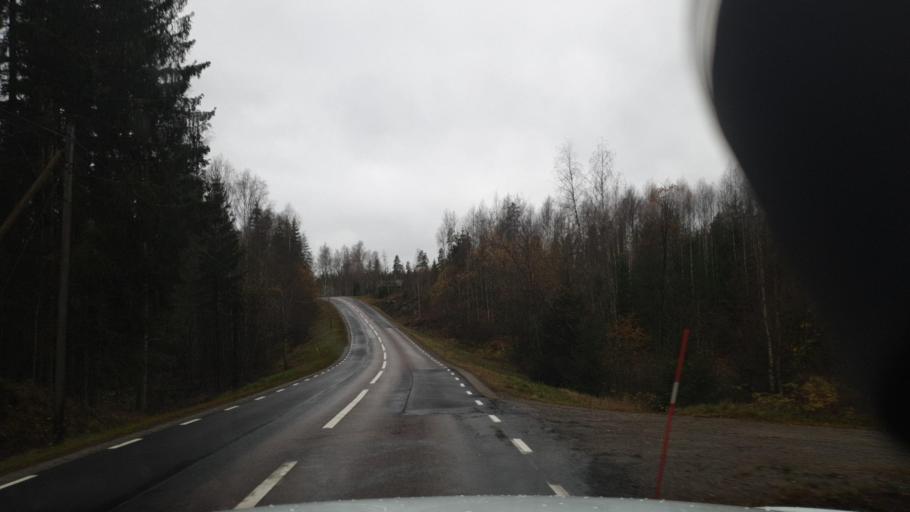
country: SE
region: Vaermland
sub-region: Sunne Kommun
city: Sunne
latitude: 59.6647
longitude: 12.9638
